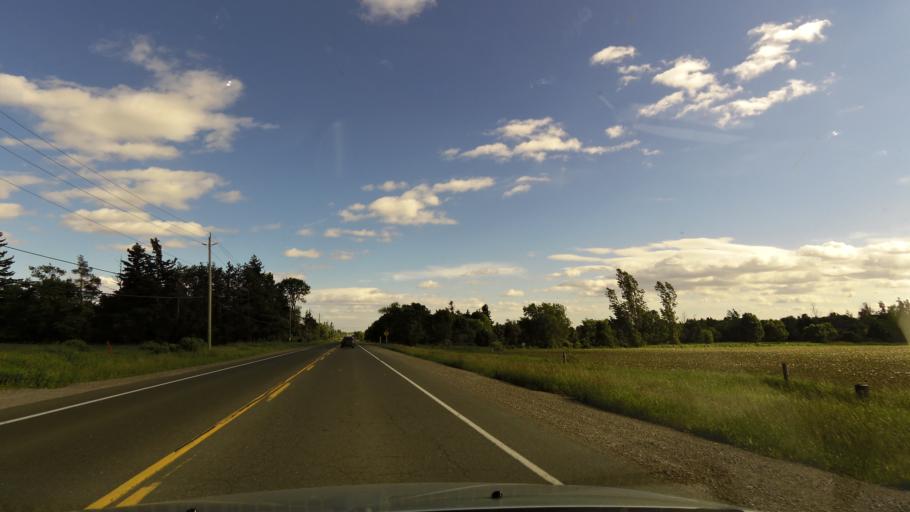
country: CA
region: Ontario
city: Vaughan
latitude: 43.8921
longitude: -79.6503
